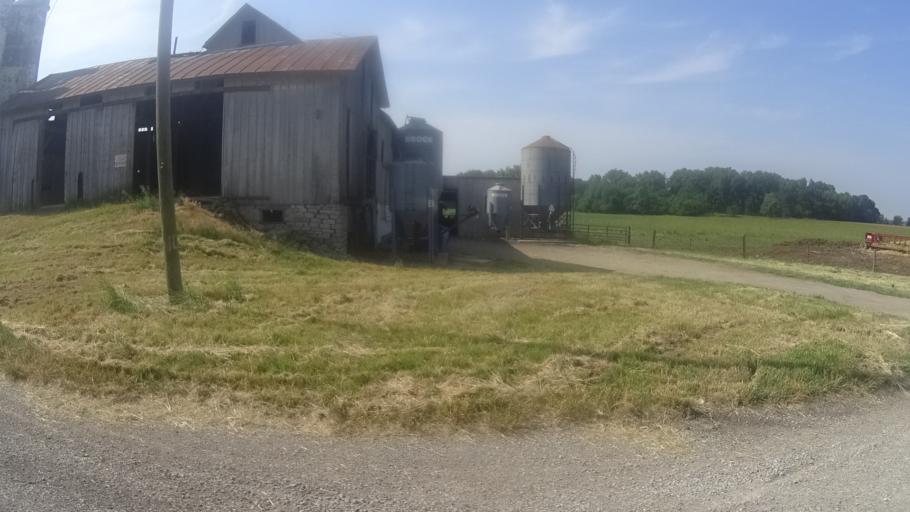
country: US
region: Ohio
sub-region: Huron County
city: Bellevue
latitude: 41.2918
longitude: -82.7681
